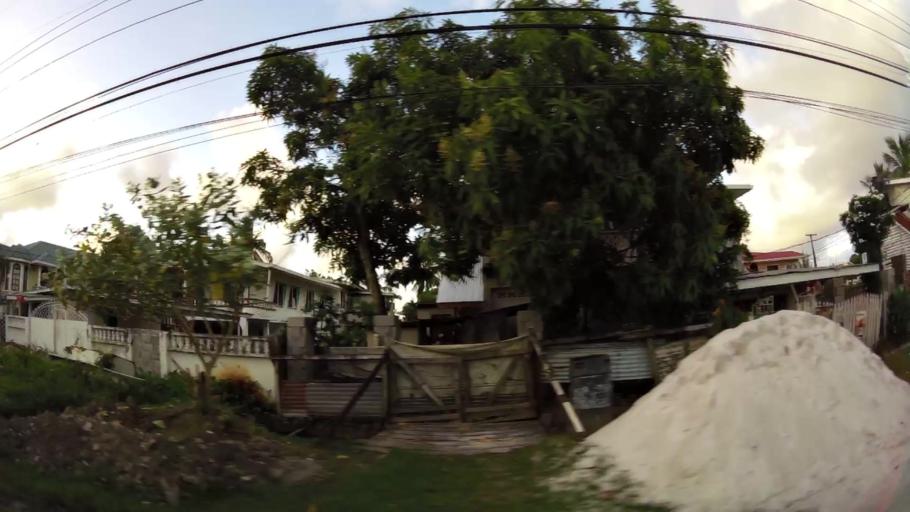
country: GY
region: Demerara-Mahaica
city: Georgetown
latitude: 6.8157
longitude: -58.1111
